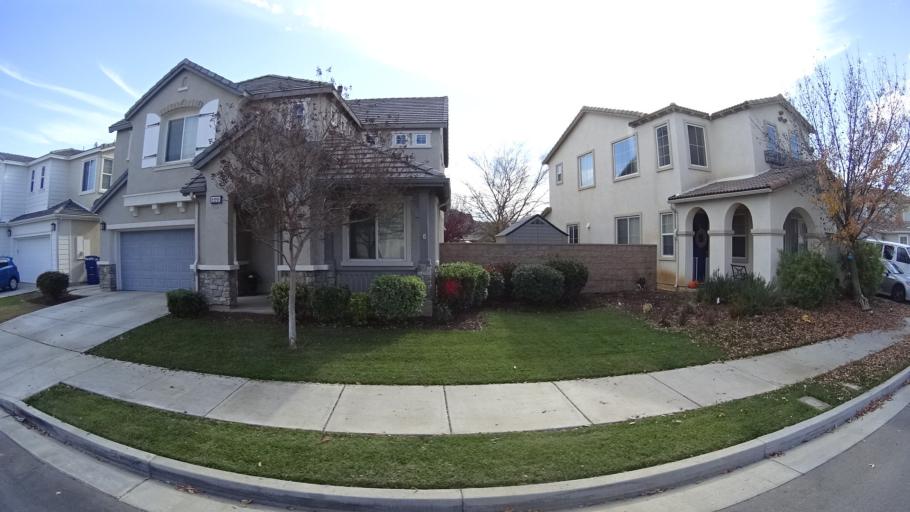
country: US
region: California
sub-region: Kern County
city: Oildale
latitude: 35.4087
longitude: -118.8798
